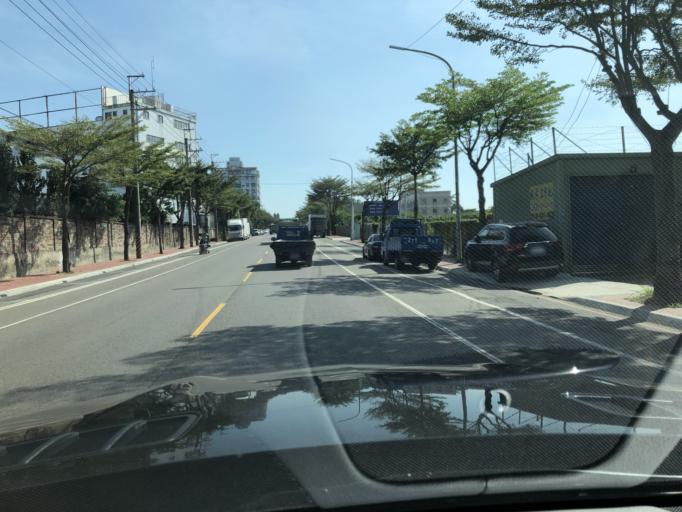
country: TW
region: Taiwan
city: Taoyuan City
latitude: 25.0696
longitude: 121.2892
